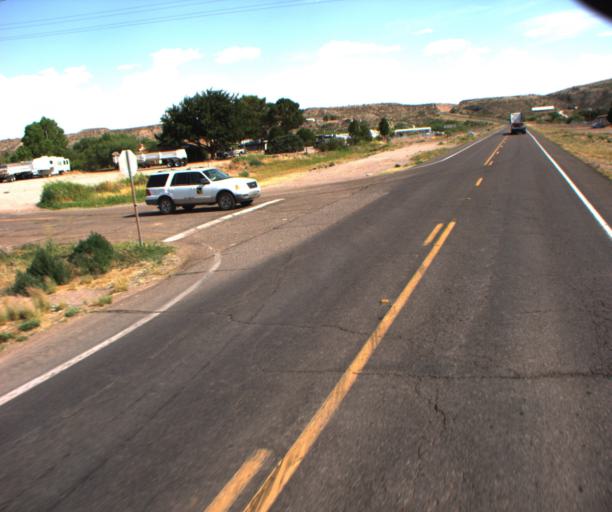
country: US
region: Arizona
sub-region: Greenlee County
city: Clifton
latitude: 32.9081
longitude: -109.1970
